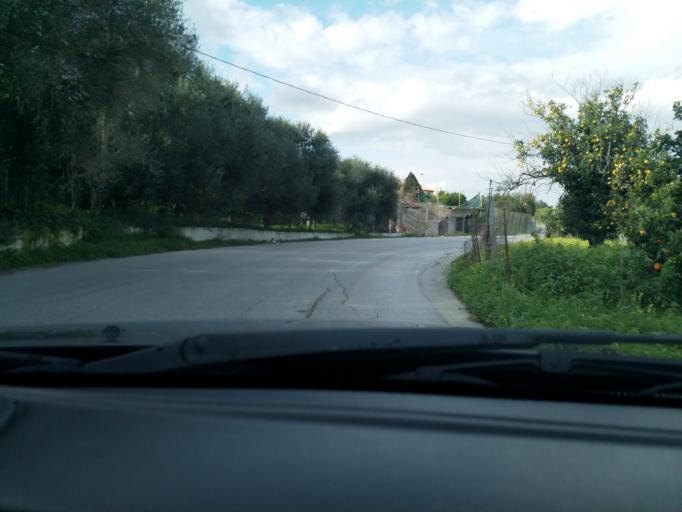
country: GR
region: Crete
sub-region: Nomos Chanias
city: Gerani
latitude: 35.5007
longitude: 23.8978
